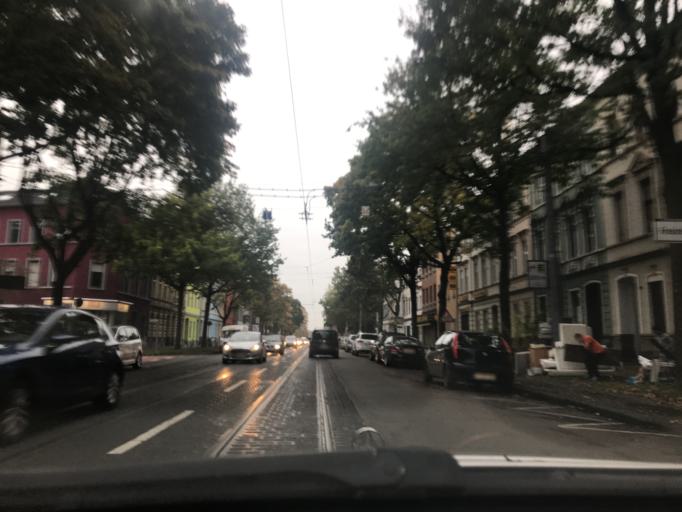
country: DE
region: North Rhine-Westphalia
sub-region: Regierungsbezirk Dusseldorf
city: Krefeld
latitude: 51.3181
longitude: 6.5747
